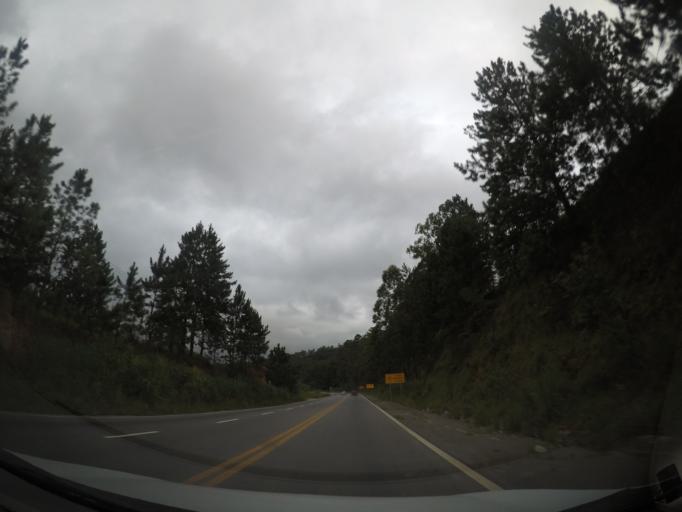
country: BR
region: Sao Paulo
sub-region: Aruja
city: Aruja
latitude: -23.3848
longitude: -46.4382
